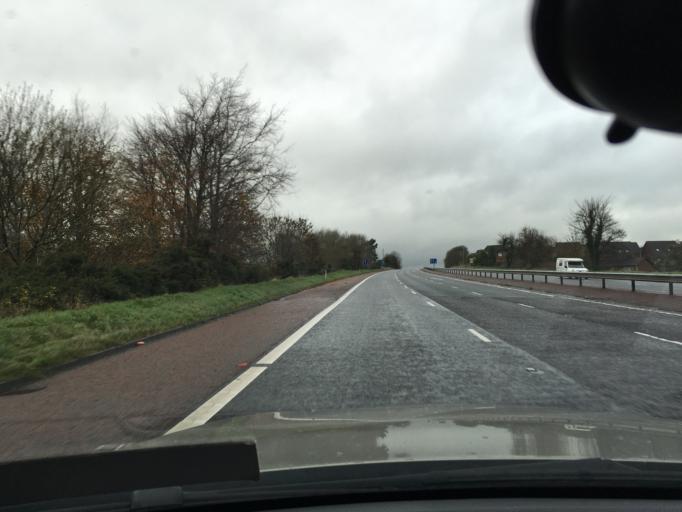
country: GB
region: Northern Ireland
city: Carnmoney
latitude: 54.6834
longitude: -5.9763
